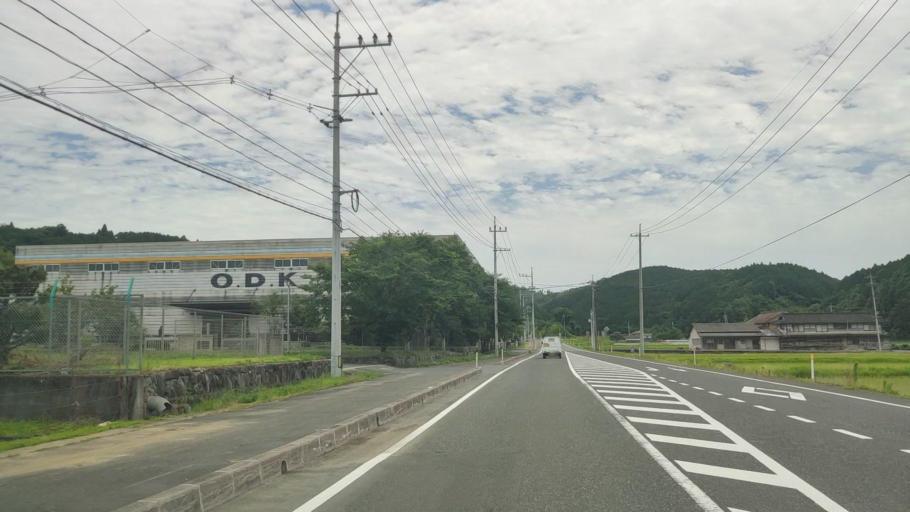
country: JP
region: Okayama
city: Tsuyama
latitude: 35.0636
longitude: 134.2095
